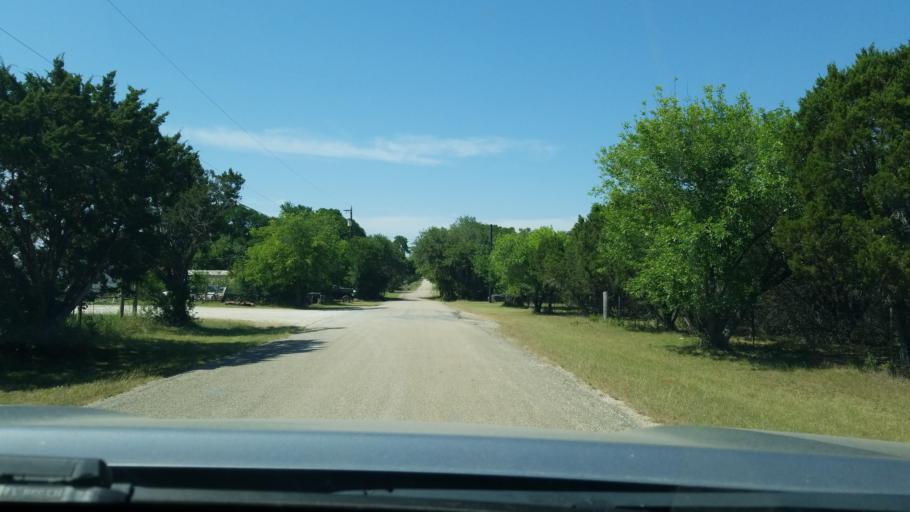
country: US
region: Texas
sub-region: Bexar County
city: Timberwood Park
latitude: 29.7481
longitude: -98.5179
